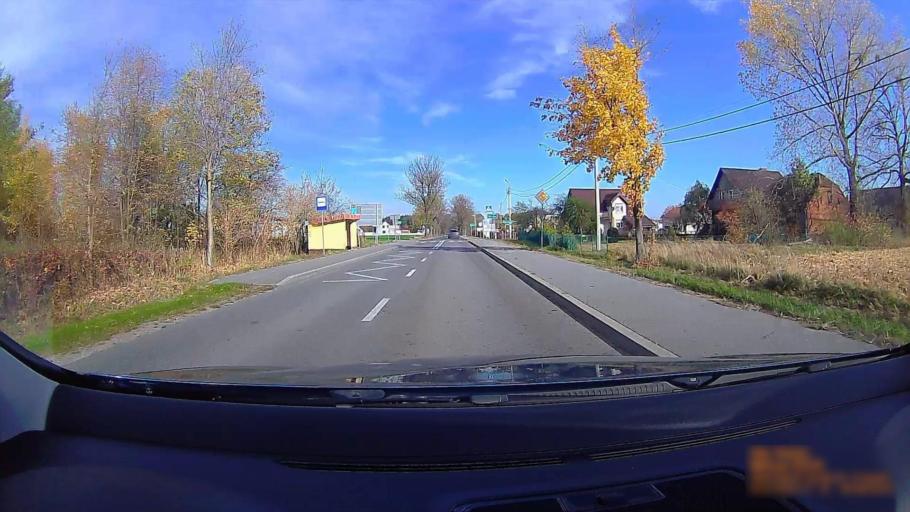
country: PL
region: Greater Poland Voivodeship
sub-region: Powiat ostrzeszowski
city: Doruchow
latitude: 51.3911
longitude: 18.0541
